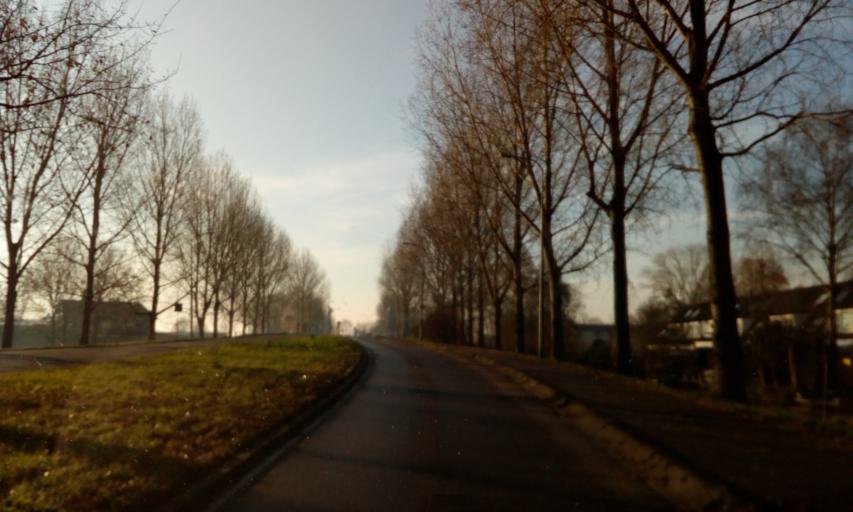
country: NL
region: South Holland
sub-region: Gemeente Vlist
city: Haastrecht
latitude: 52.0059
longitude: 4.7444
